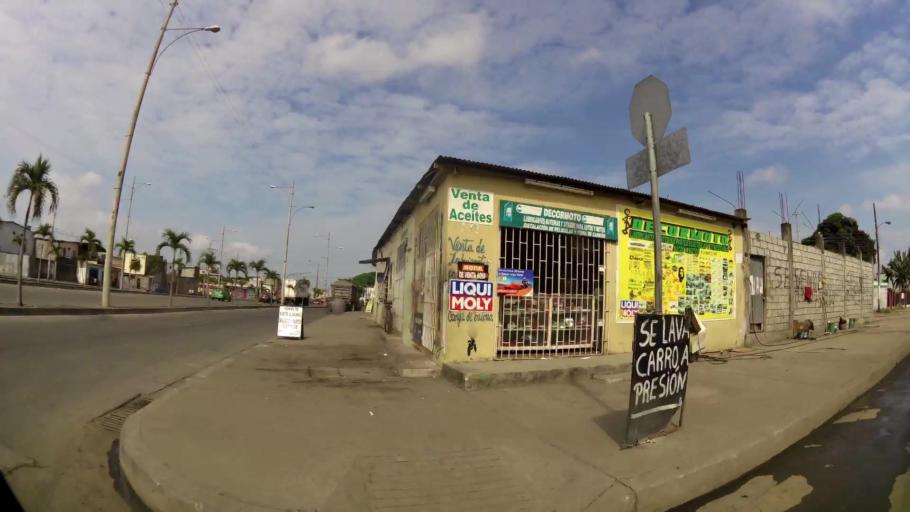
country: EC
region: Guayas
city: Guayaquil
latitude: -2.2608
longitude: -79.8913
